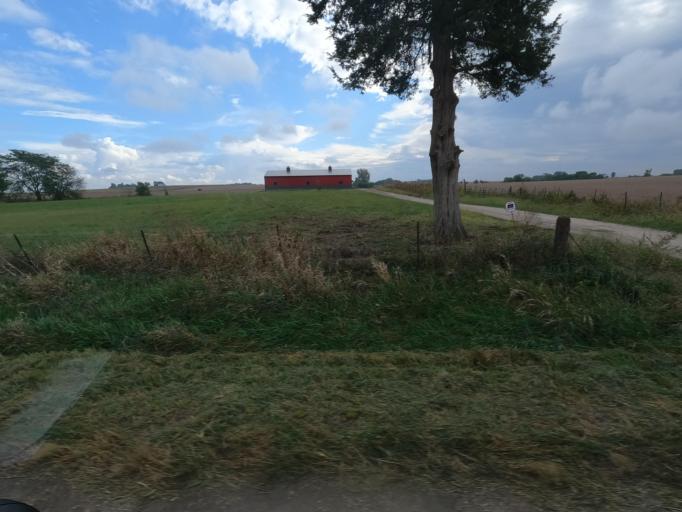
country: US
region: Iowa
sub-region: Henry County
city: Mount Pleasant
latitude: 40.7845
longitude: -91.5725
